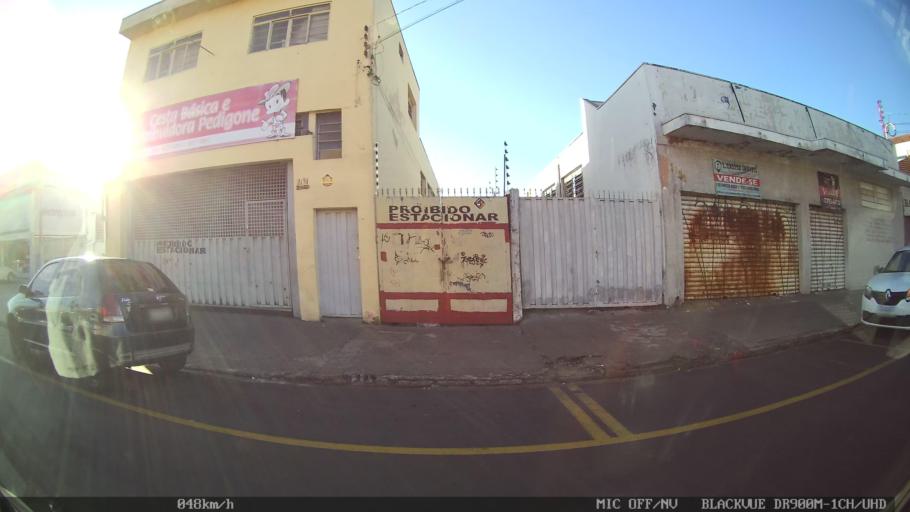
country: BR
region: Sao Paulo
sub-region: Franca
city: Franca
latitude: -20.5258
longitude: -47.3710
